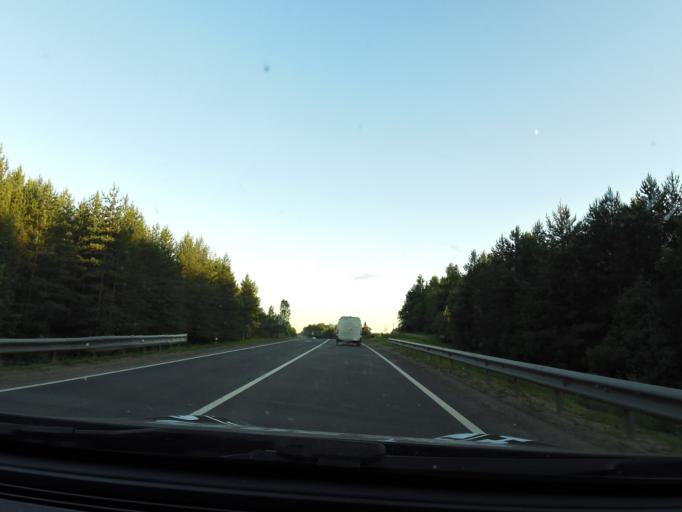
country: RU
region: Jaroslavl
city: Prechistoye
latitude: 58.4808
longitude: 40.3231
